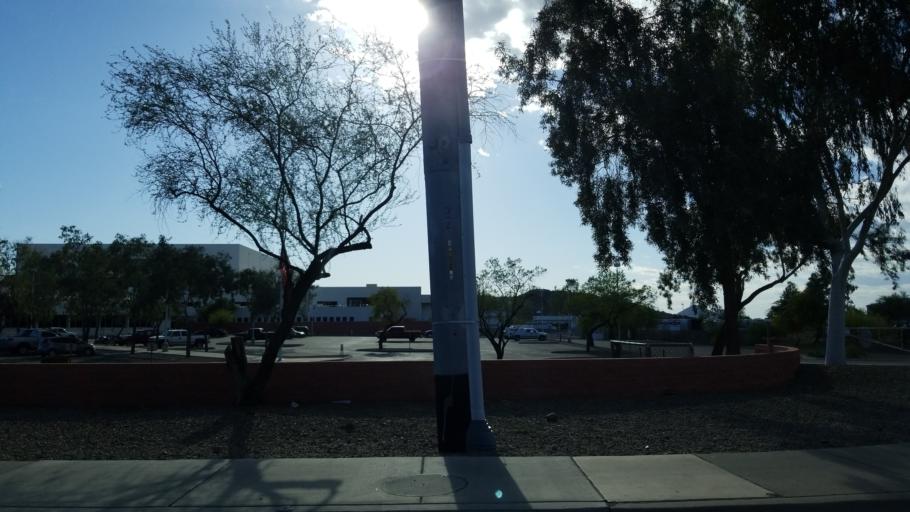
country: US
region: Arizona
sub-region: Maricopa County
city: Glendale
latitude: 33.6923
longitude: -112.1001
